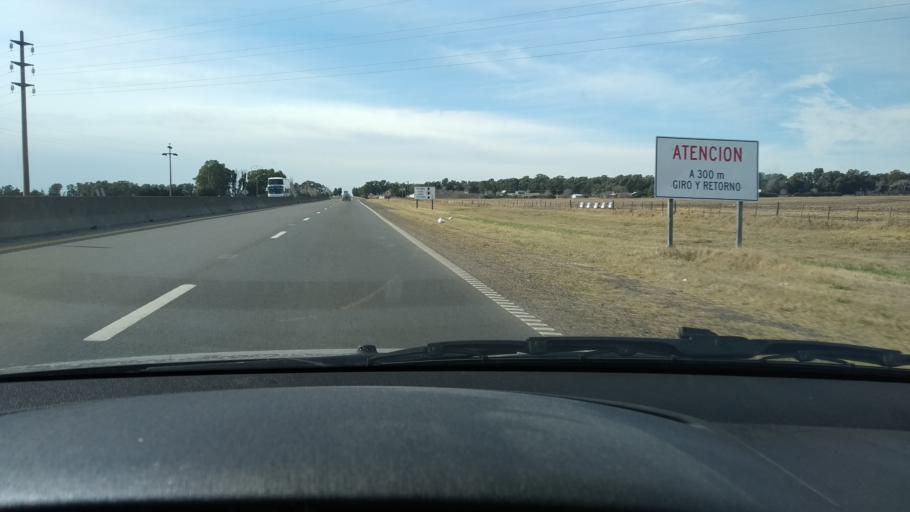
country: AR
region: Buenos Aires
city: Olavarria
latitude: -36.9032
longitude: -60.1869
